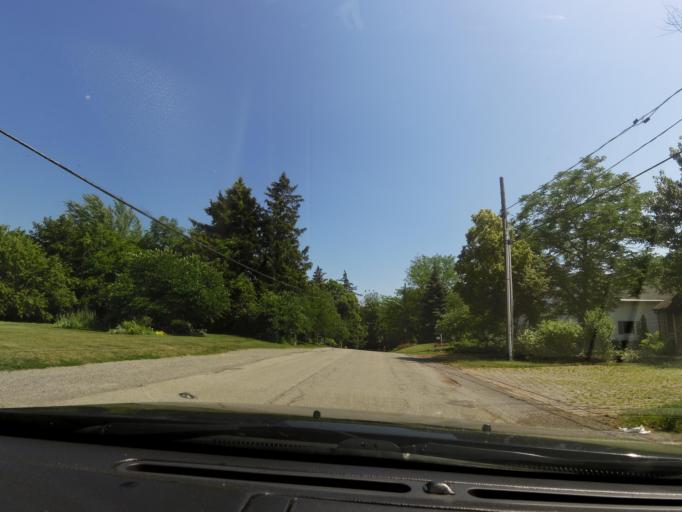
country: US
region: New York
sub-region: Niagara County
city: Lewiston
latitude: 43.1700
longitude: -79.0573
